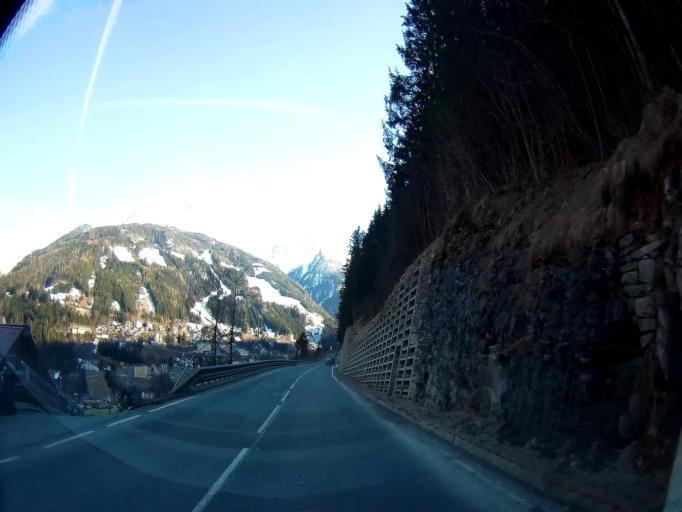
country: AT
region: Salzburg
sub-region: Politischer Bezirk Sankt Johann im Pongau
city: Bad Gastein
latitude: 47.1303
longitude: 13.1296
